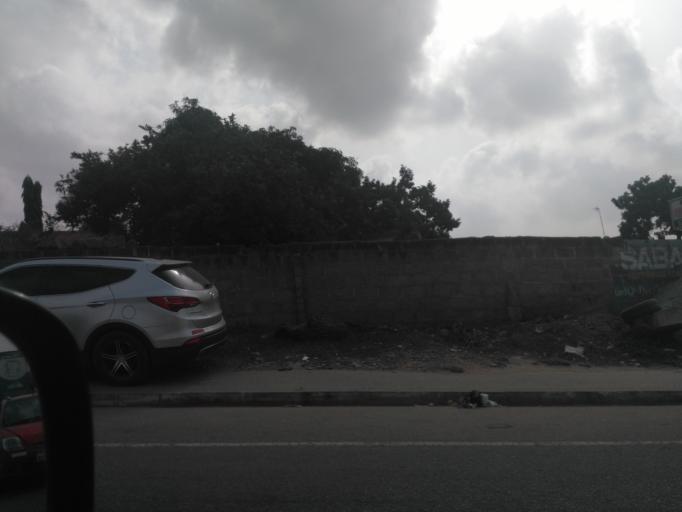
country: GH
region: Greater Accra
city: Accra
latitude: 5.5831
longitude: -0.1942
